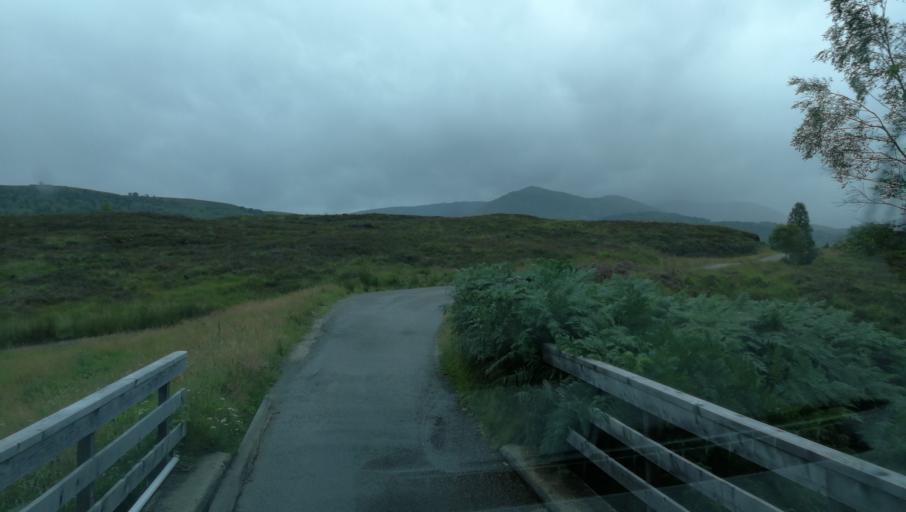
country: GB
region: Scotland
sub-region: Highland
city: Spean Bridge
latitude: 57.2729
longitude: -4.9621
